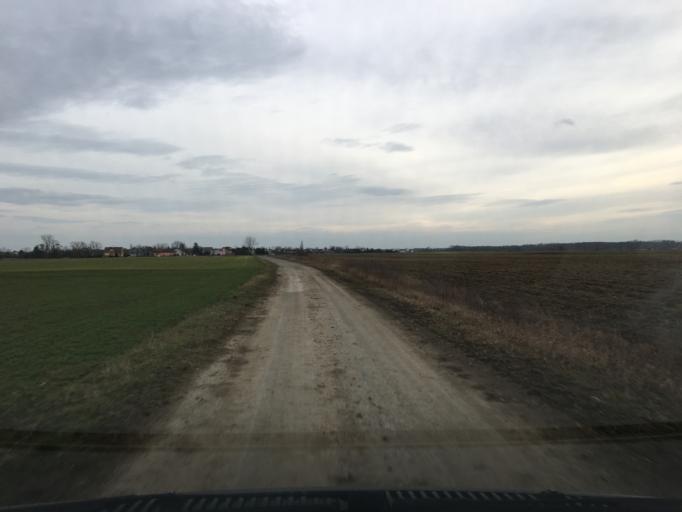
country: PL
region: Opole Voivodeship
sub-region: Powiat kedzierzynsko-kozielski
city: Wiekszyce
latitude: 50.3637
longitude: 18.1136
